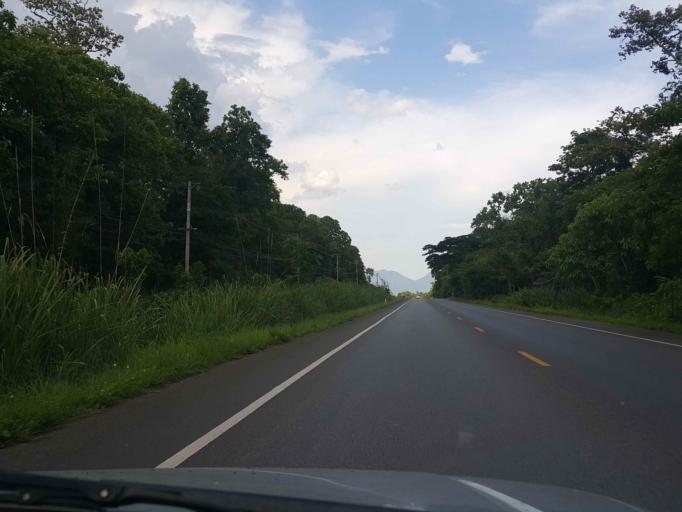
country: TH
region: Lampang
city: Wang Nuea
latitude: 19.1646
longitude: 99.5682
